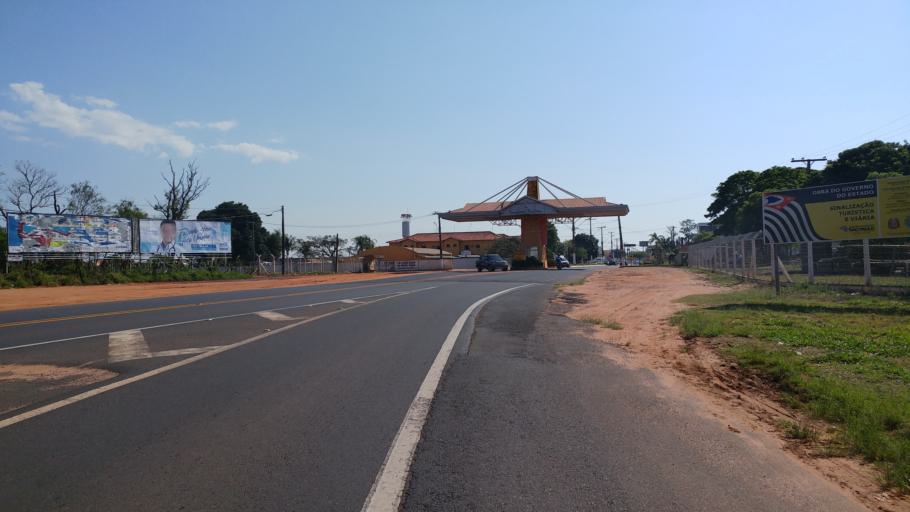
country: BR
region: Sao Paulo
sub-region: Paraguacu Paulista
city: Paraguacu Paulista
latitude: -22.4314
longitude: -50.5862
